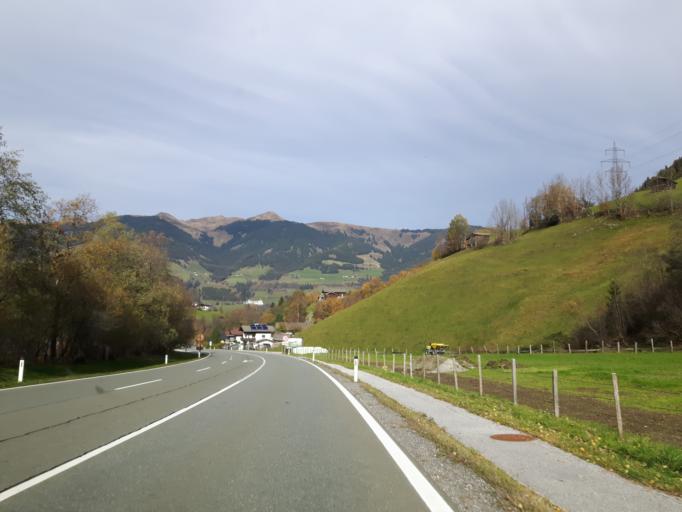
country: AT
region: Salzburg
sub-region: Politischer Bezirk Zell am See
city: Mittersill
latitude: 47.2780
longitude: 12.4880
